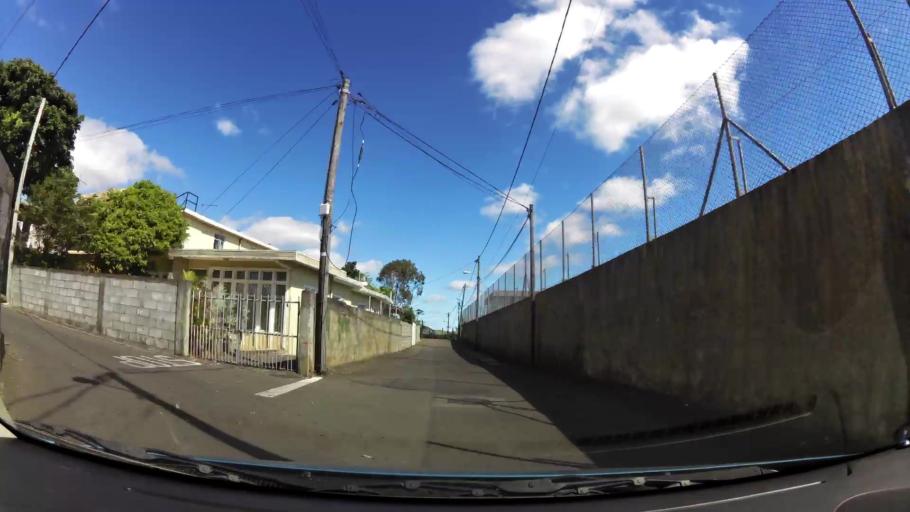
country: MU
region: Plaines Wilhems
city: Vacoas
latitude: -20.2918
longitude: 57.4773
